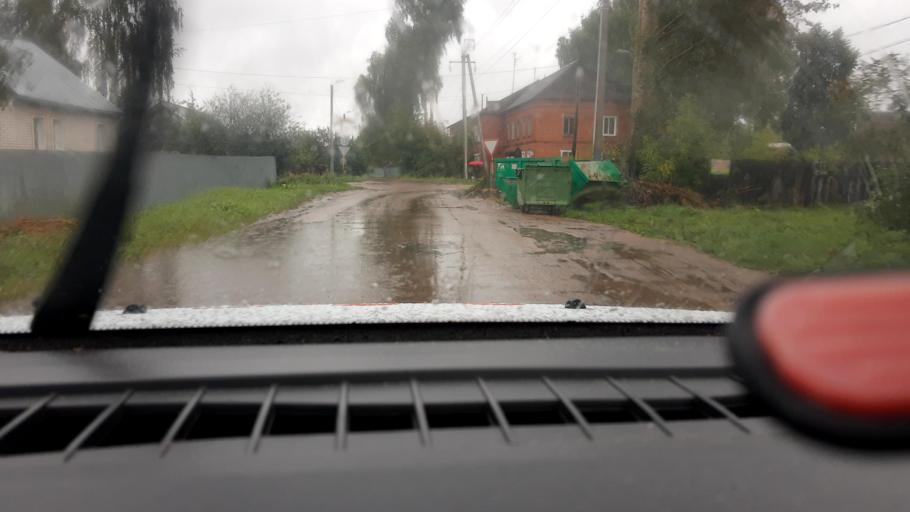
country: RU
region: Nizjnij Novgorod
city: Lyskovo
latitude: 56.0292
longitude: 45.0281
